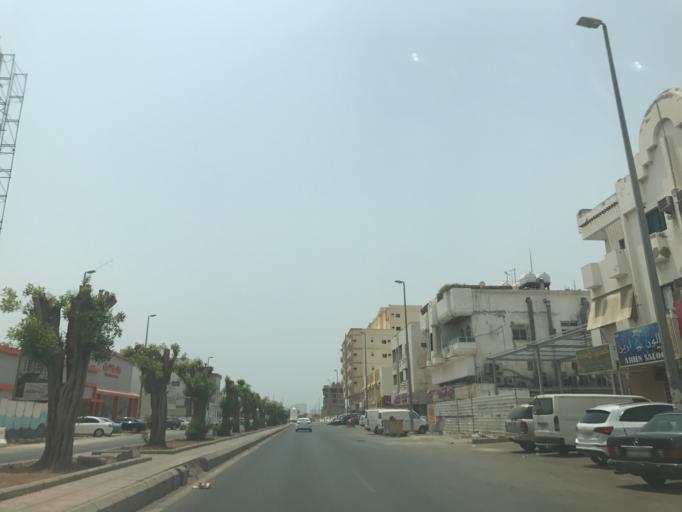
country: SA
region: Makkah
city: Jeddah
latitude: 21.5827
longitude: 39.1520
